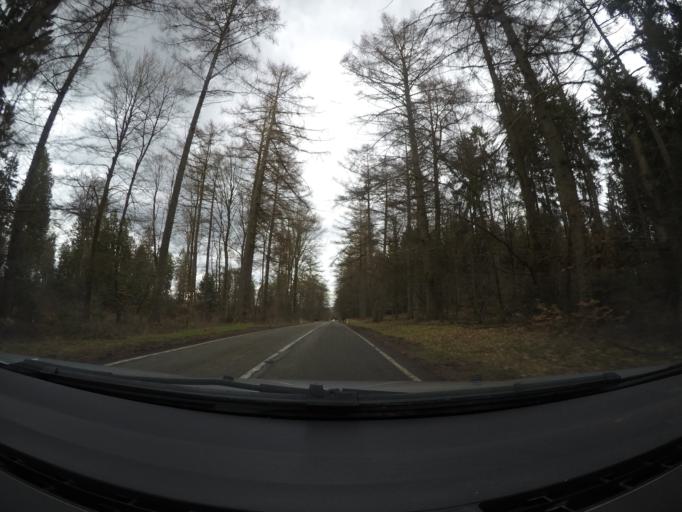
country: BE
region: Wallonia
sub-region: Province du Luxembourg
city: Leglise
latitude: 49.7637
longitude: 5.4911
